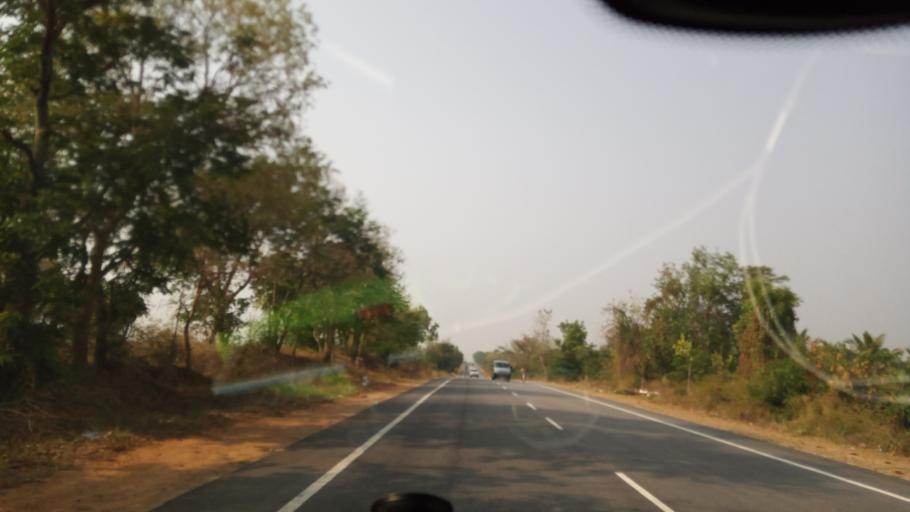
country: IN
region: Karnataka
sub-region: Mandya
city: Belluru
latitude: 12.9247
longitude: 76.7487
